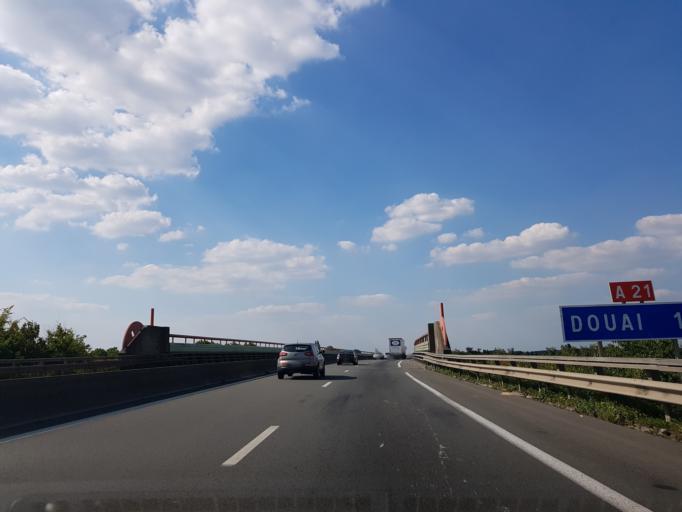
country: FR
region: Nord-Pas-de-Calais
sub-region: Departement du Nord
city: Somain
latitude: 50.3537
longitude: 3.2626
